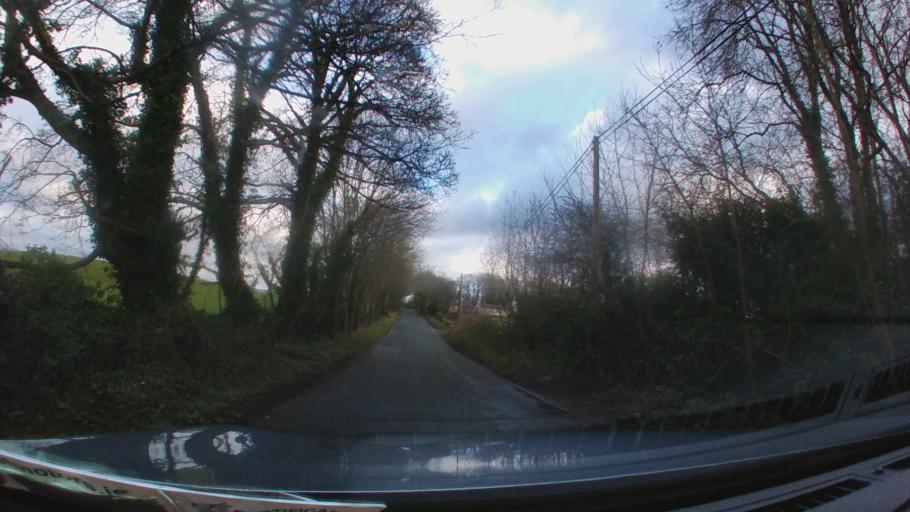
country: IE
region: Leinster
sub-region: Kilkenny
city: Thomastown
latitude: 52.5554
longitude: -7.1223
